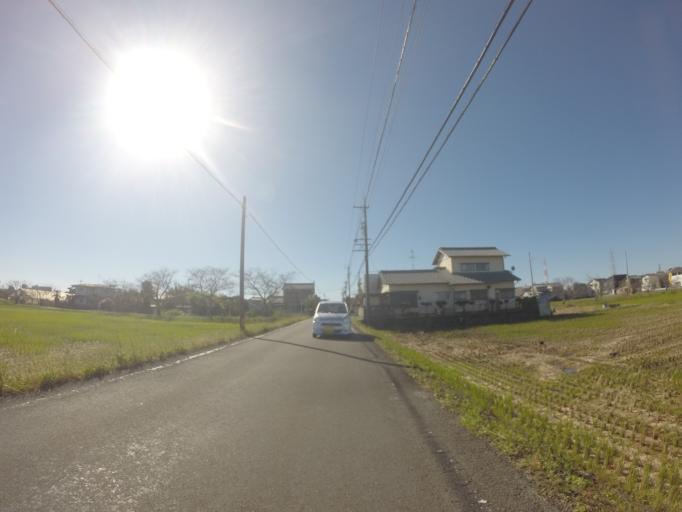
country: JP
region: Shizuoka
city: Fujieda
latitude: 34.8307
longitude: 138.2390
